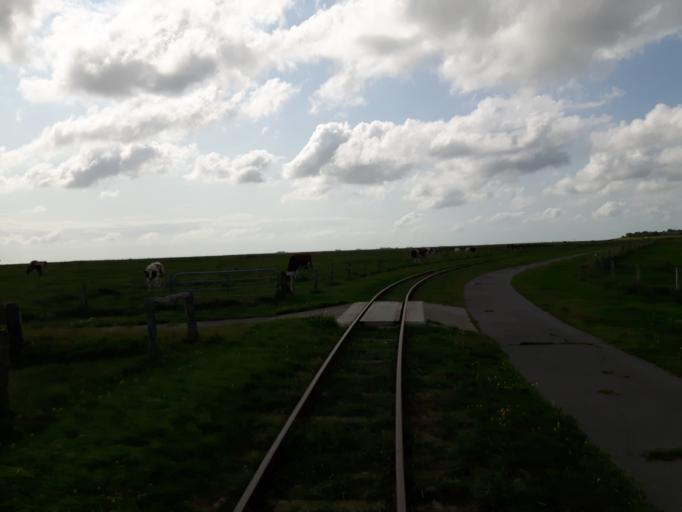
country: DE
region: Schleswig-Holstein
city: Grode
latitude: 54.6761
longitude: 8.7022
